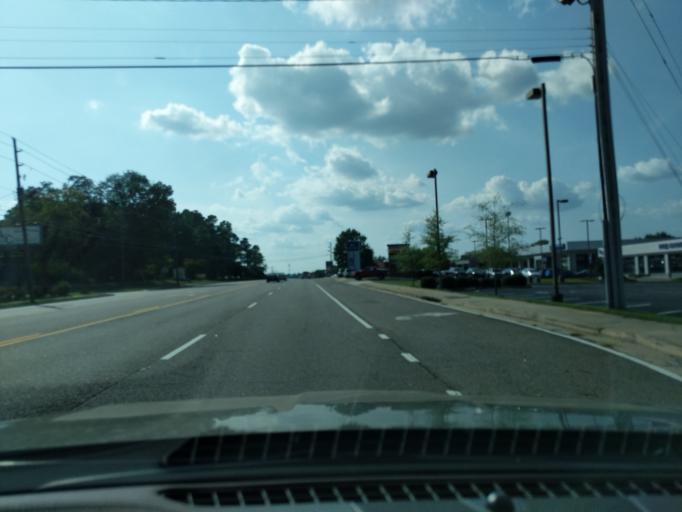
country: US
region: Georgia
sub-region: Columbia County
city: Martinez
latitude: 33.5150
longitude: -82.0629
